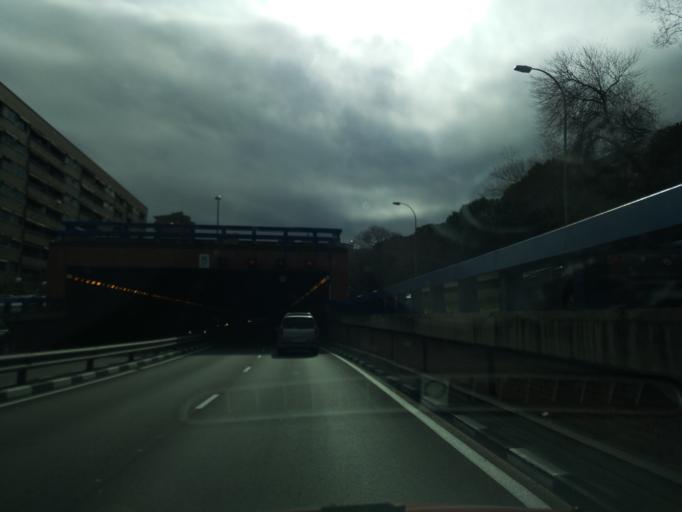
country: ES
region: Madrid
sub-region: Provincia de Madrid
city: Ciudad Lineal
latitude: 40.4657
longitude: -3.6580
